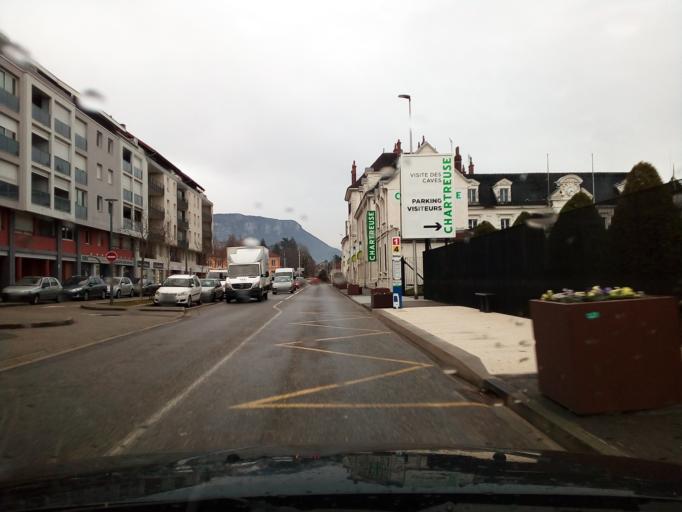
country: FR
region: Rhone-Alpes
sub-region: Departement de l'Isere
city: Voiron
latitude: 45.3625
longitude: 5.5979
